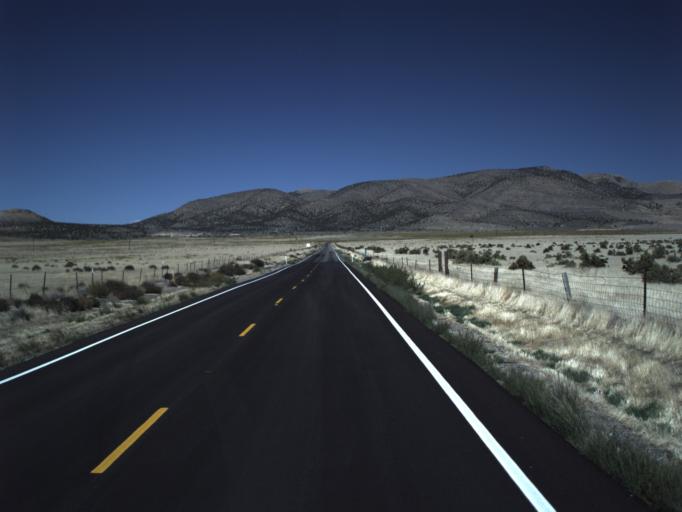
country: US
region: Utah
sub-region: Utah County
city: Eagle Mountain
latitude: 40.1512
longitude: -111.9496
